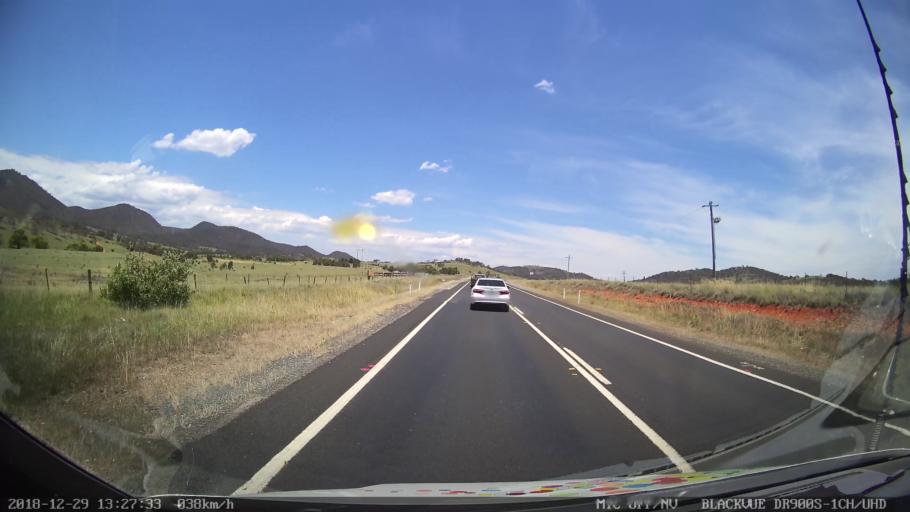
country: AU
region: New South Wales
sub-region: Cooma-Monaro
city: Cooma
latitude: -35.8667
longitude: 149.1598
